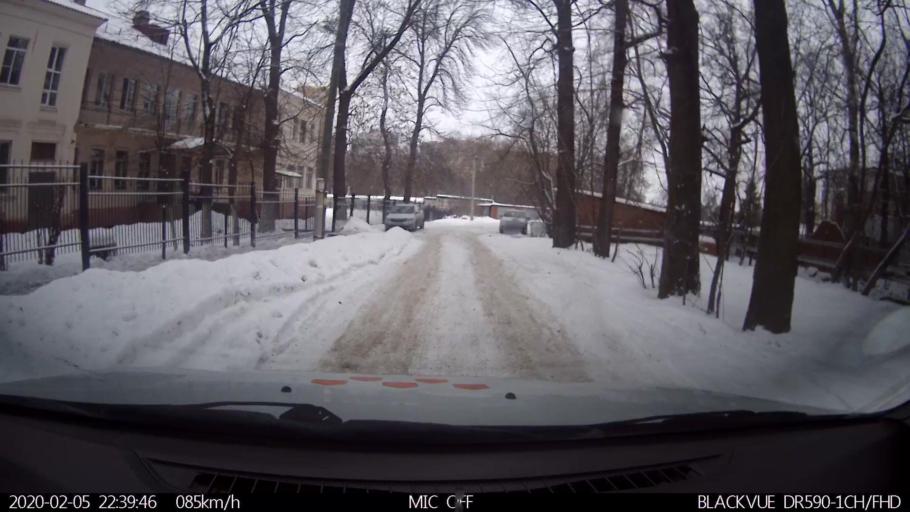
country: RU
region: Nizjnij Novgorod
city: Imeni Stepana Razina
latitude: 54.7258
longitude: 44.3074
